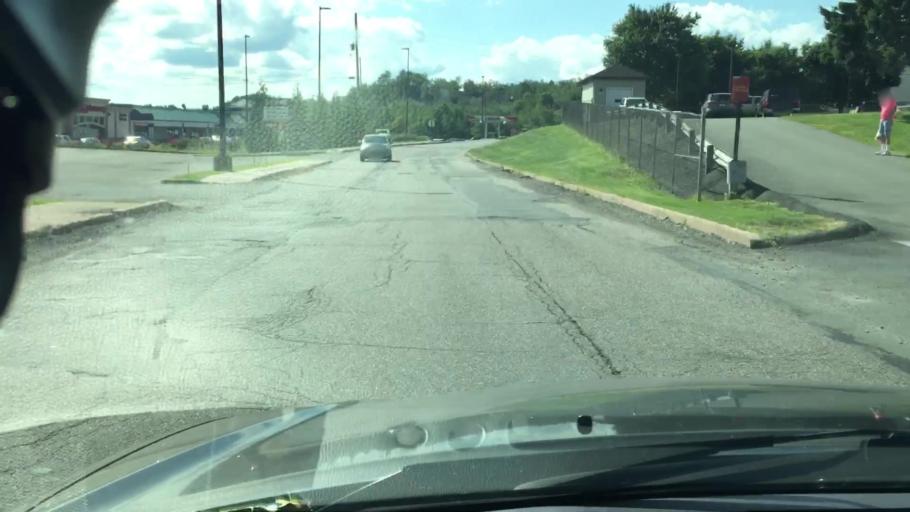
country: US
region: Pennsylvania
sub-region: Luzerne County
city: Hazleton
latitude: 40.9544
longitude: -75.9796
